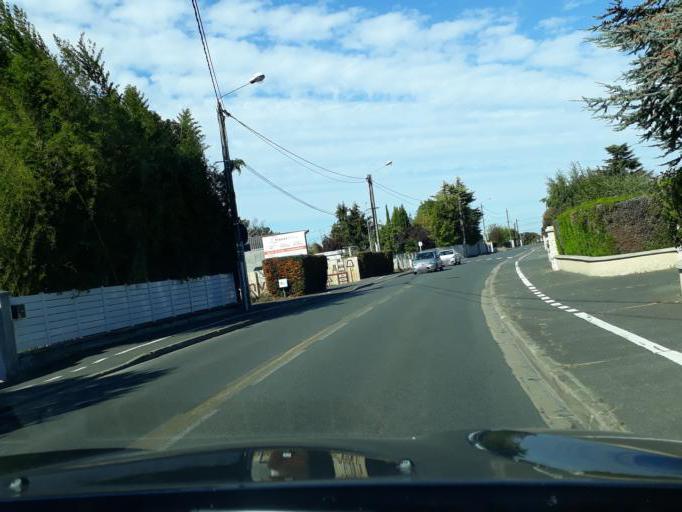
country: FR
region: Centre
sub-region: Departement d'Indre-et-Loire
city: Saint-Avertin
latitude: 47.3445
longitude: 0.7356
